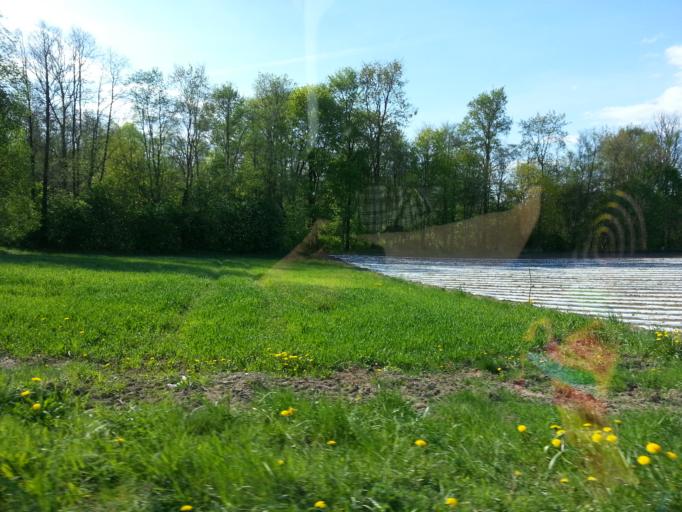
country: LT
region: Panevezys
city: Pasvalys
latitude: 56.0338
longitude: 24.3609
